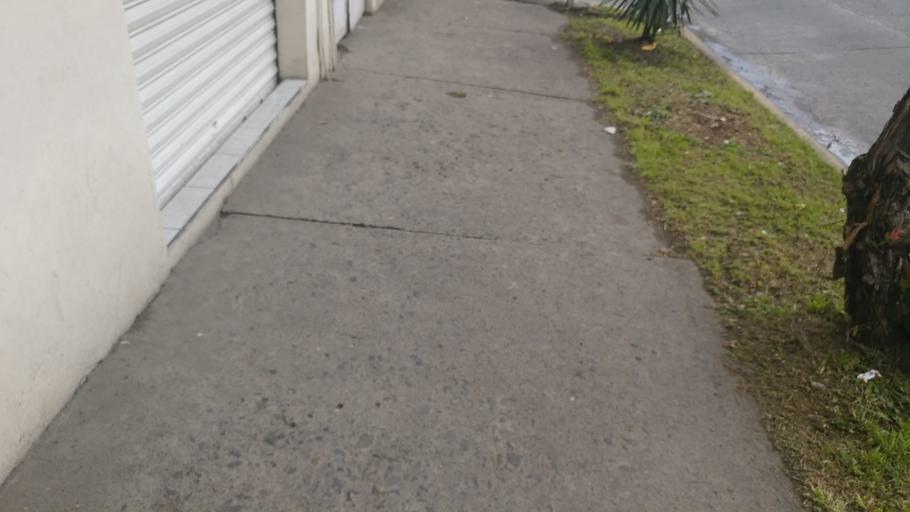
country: MX
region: Veracruz
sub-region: Xalapa
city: Xalapa de Enriquez
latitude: 19.5366
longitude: -96.9201
